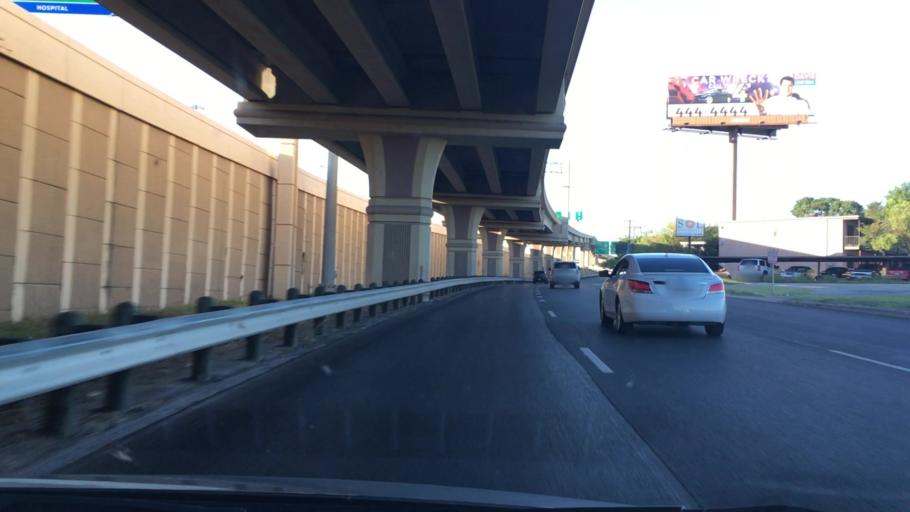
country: US
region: Texas
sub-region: Bexar County
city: Balcones Heights
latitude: 29.4949
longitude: -98.5473
